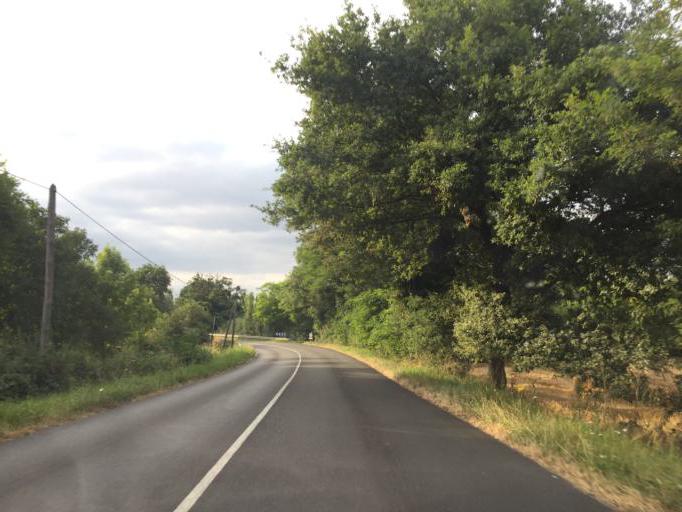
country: FR
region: Auvergne
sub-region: Departement de l'Allier
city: Yzeure
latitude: 46.5465
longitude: 3.3751
